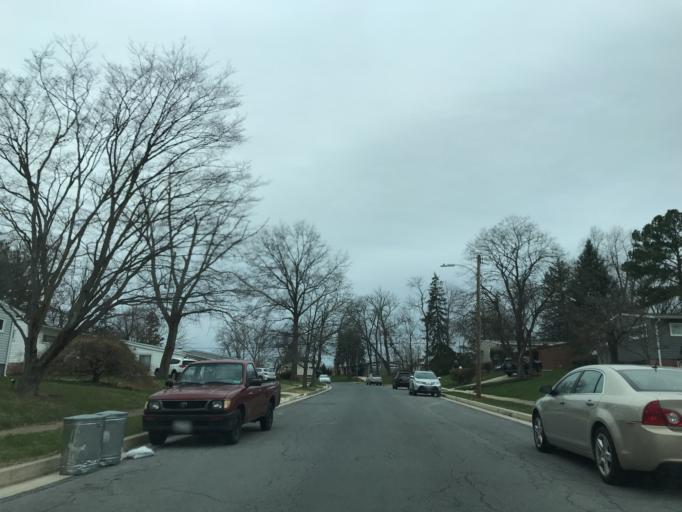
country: US
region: Maryland
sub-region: Baltimore County
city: Pikesville
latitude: 39.3786
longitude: -76.6792
